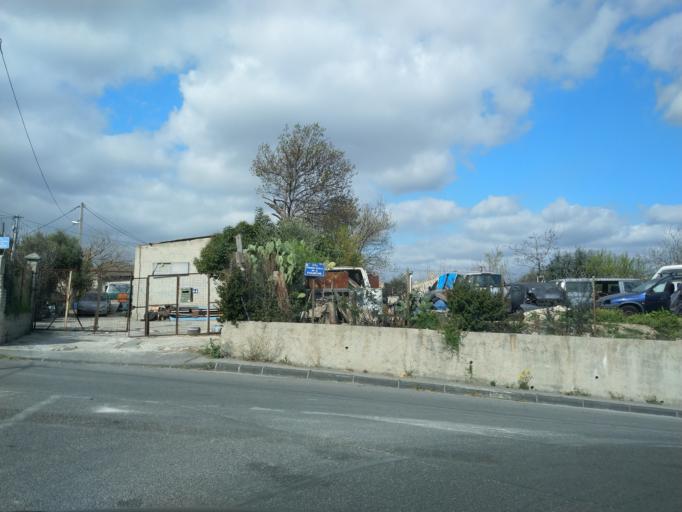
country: FR
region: Provence-Alpes-Cote d'Azur
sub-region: Departement des Bouches-du-Rhone
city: Plan-de-Cuques
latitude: 43.3274
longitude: 5.4542
